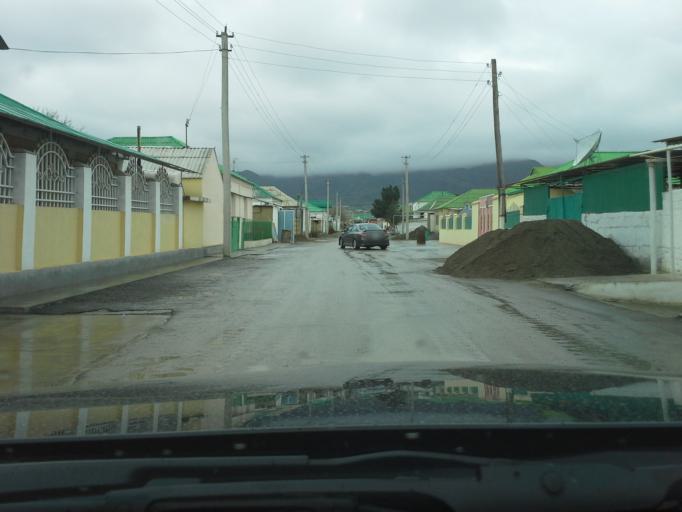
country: TM
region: Ahal
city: Abadan
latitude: 37.9701
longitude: 58.2119
